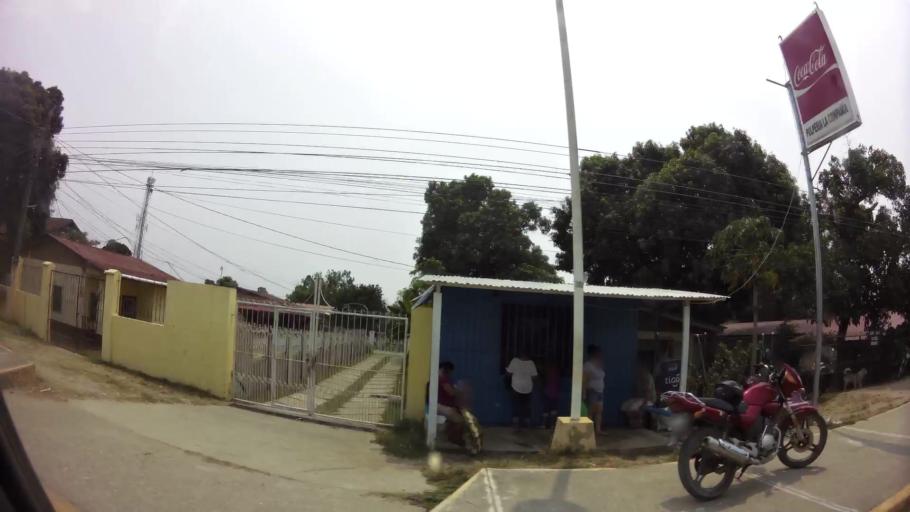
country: HN
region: Yoro
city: El Progreso
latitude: 15.3927
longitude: -87.8113
